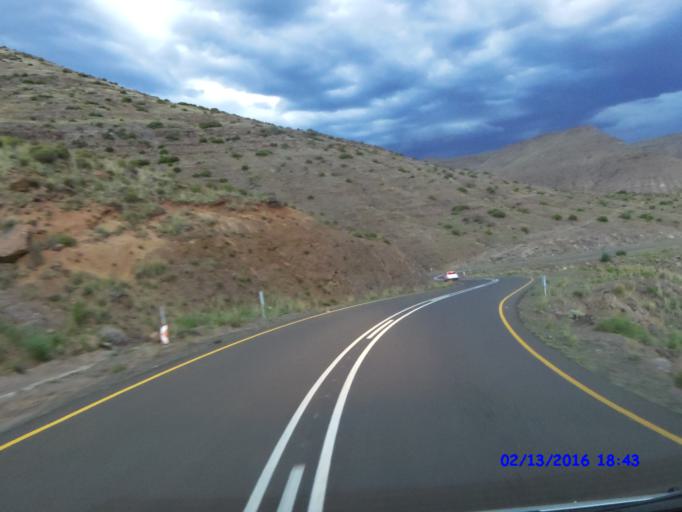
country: LS
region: Qacha's Nek
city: Qacha's Nek
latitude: -30.0476
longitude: 28.3074
